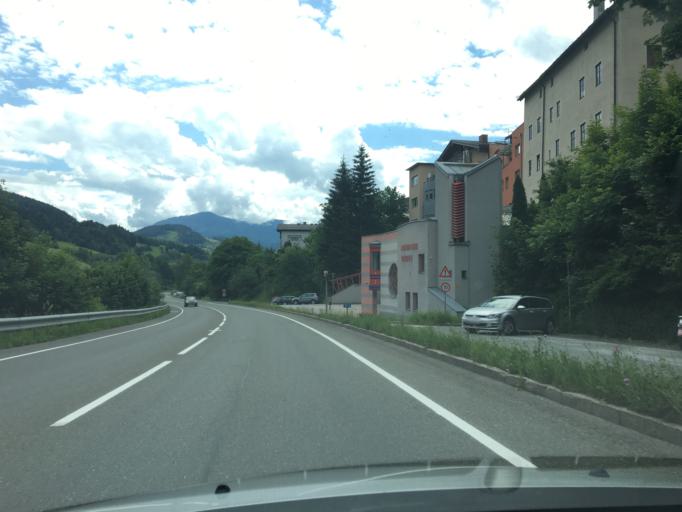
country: AT
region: Salzburg
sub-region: Politischer Bezirk Sankt Johann im Pongau
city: Werfen
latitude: 47.4779
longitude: 13.1889
